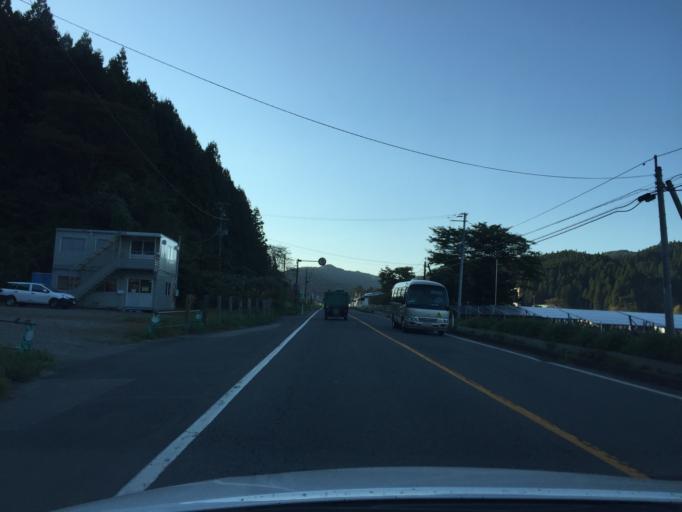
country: JP
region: Fukushima
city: Iwaki
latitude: 37.1396
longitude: 140.6904
